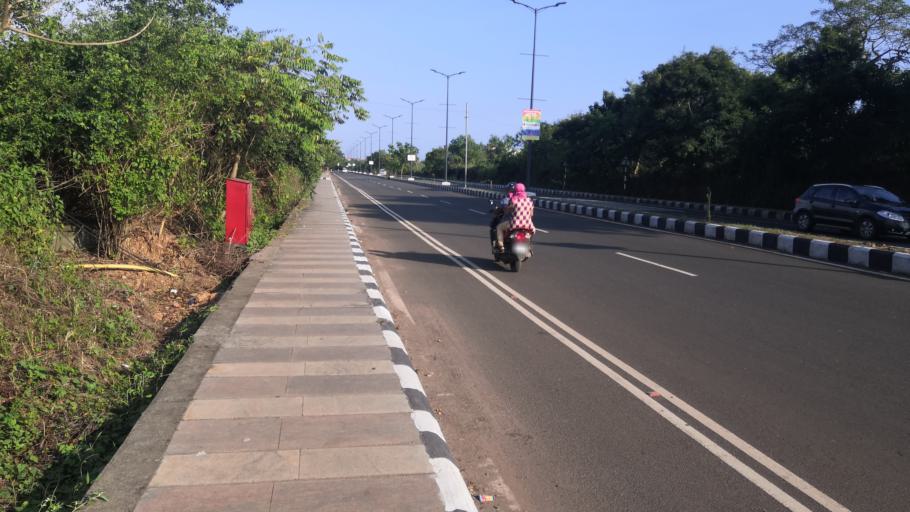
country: IN
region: Goa
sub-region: North Goa
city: Taleigao
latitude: 15.4593
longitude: 73.8231
